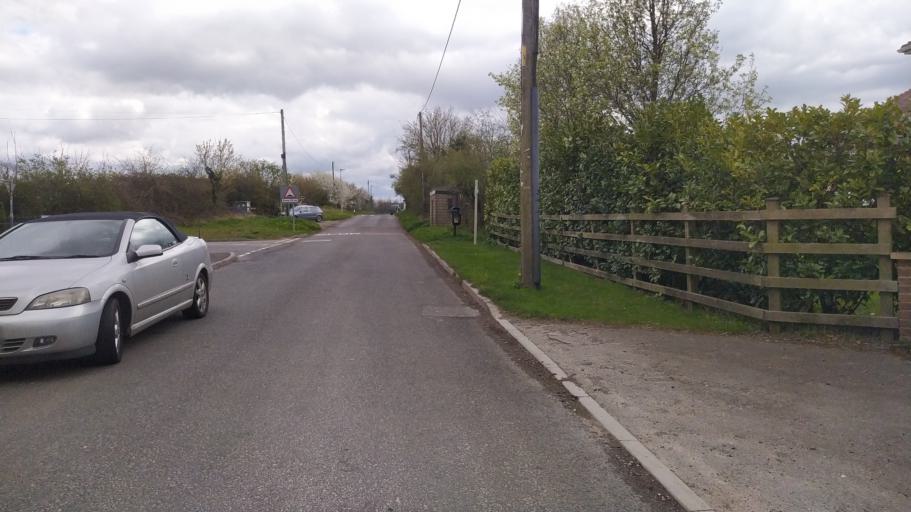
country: GB
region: England
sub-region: Wiltshire
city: North Bradley
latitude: 51.2959
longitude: -2.1713
